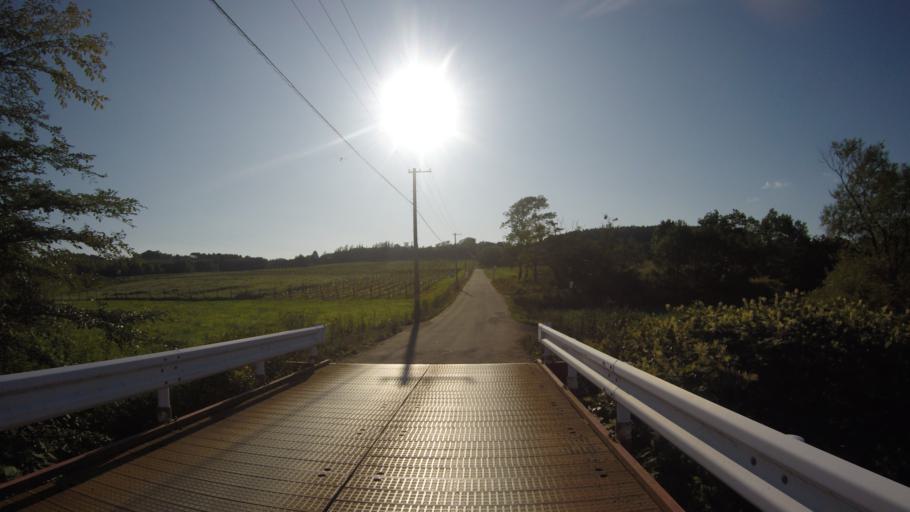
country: JP
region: Hokkaido
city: Iwamizawa
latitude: 43.1929
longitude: 141.8235
